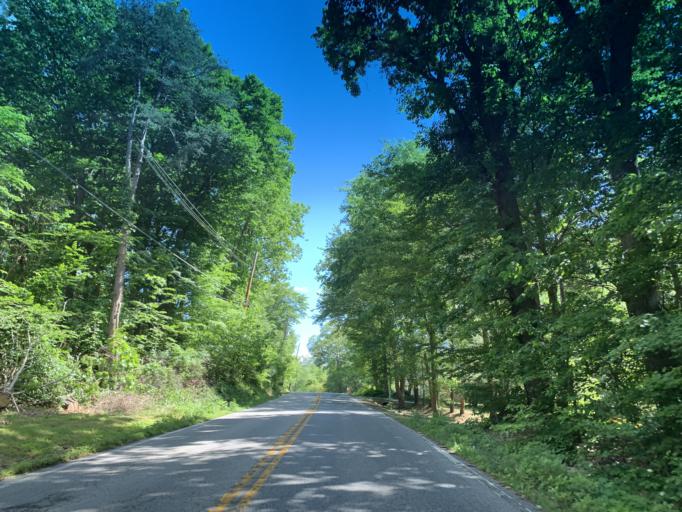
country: US
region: Maryland
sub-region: Cecil County
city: Elkton
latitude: 39.5968
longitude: -75.8643
